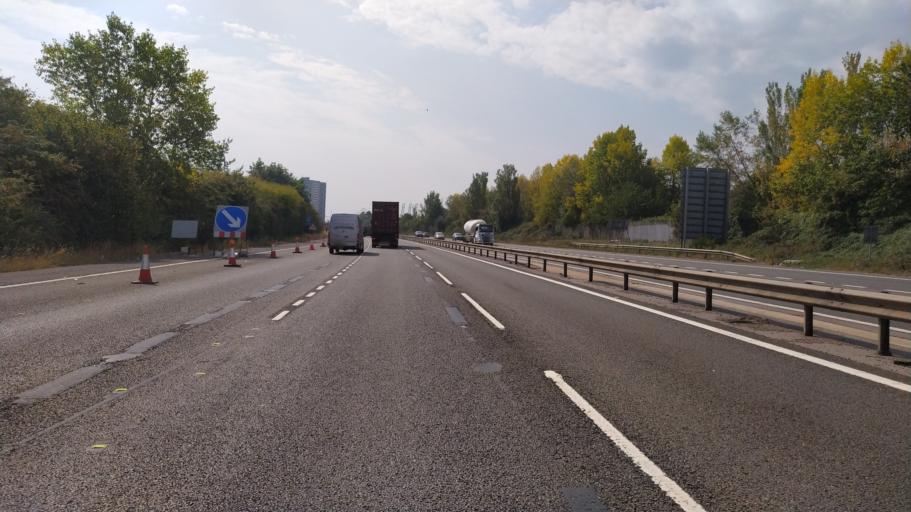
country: GB
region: England
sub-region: Hampshire
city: Totton
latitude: 50.9291
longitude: -1.4728
